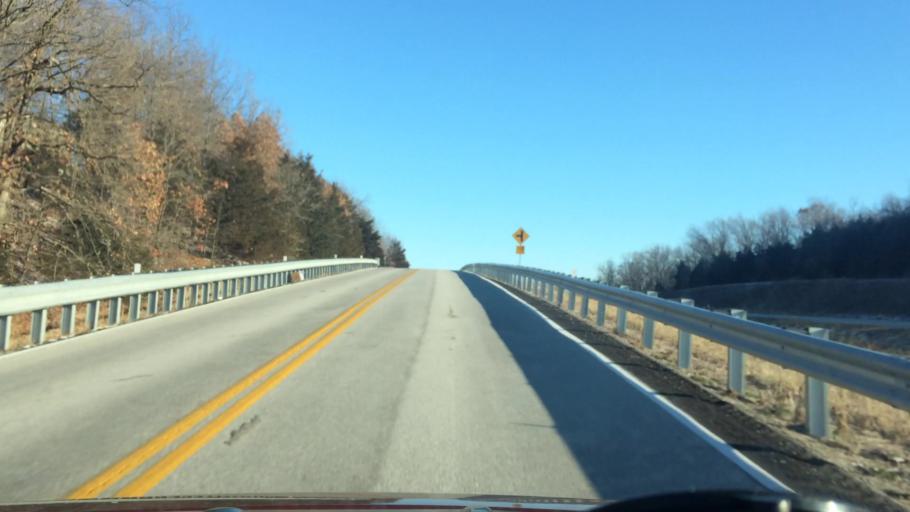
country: US
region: Missouri
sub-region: Greene County
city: Strafford
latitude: 37.2772
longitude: -93.0474
